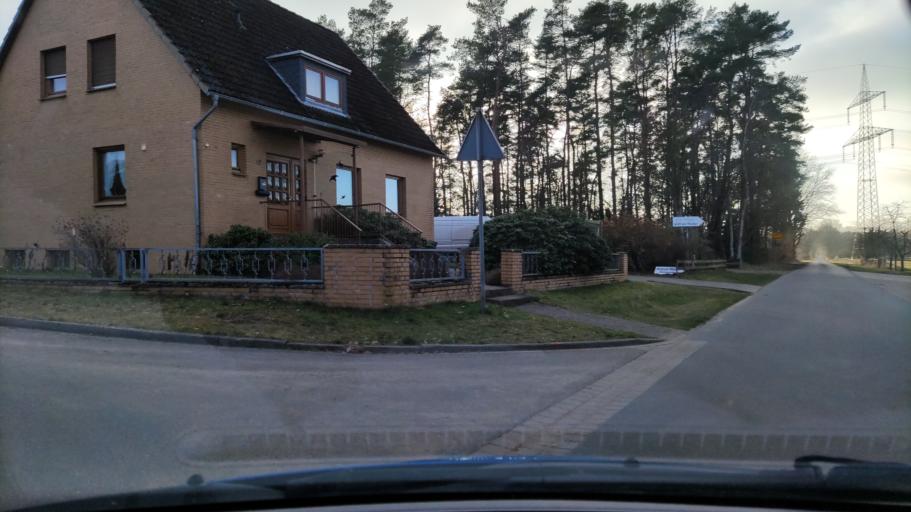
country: DE
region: Lower Saxony
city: Gerdau
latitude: 52.9700
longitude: 10.3880
